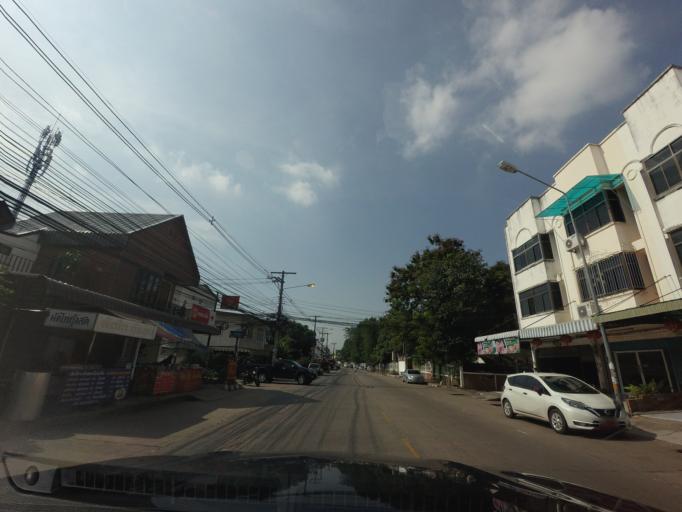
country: TH
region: Khon Kaen
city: Khon Kaen
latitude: 16.4221
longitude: 102.8499
